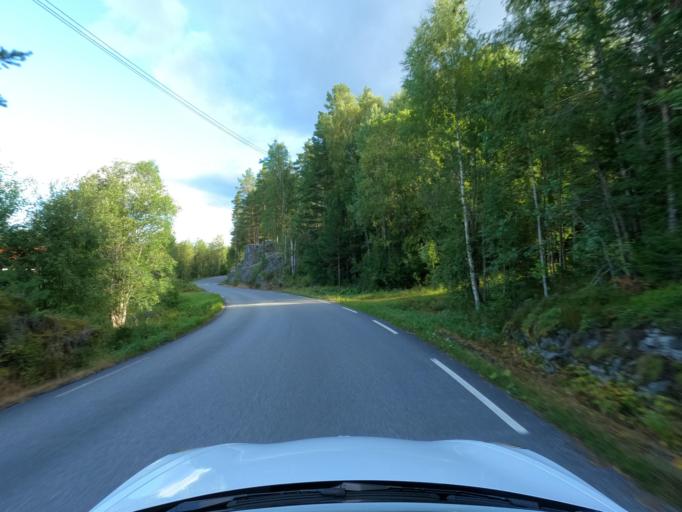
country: NO
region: Telemark
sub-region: Hjartdal
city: Sauland
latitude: 59.7850
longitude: 9.1019
